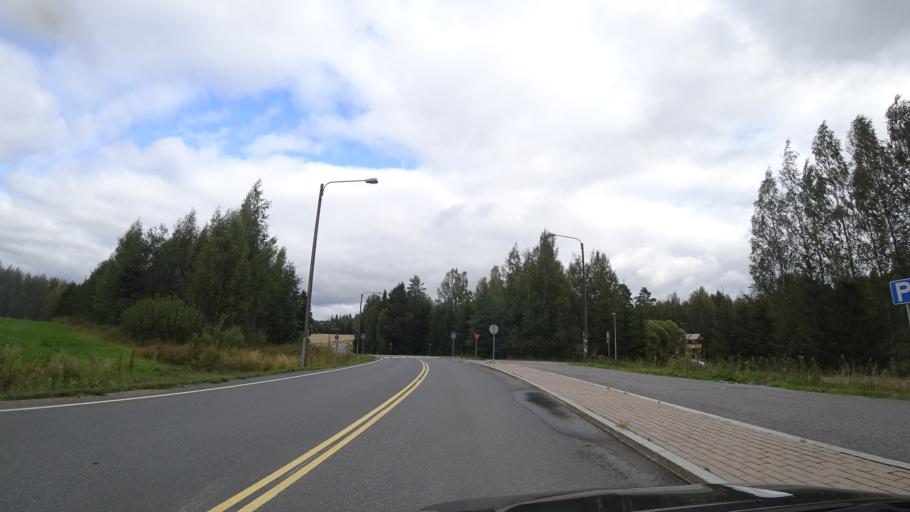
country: FI
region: Haeme
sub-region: Haemeenlinna
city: Lammi
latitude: 61.0538
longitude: 25.0062
